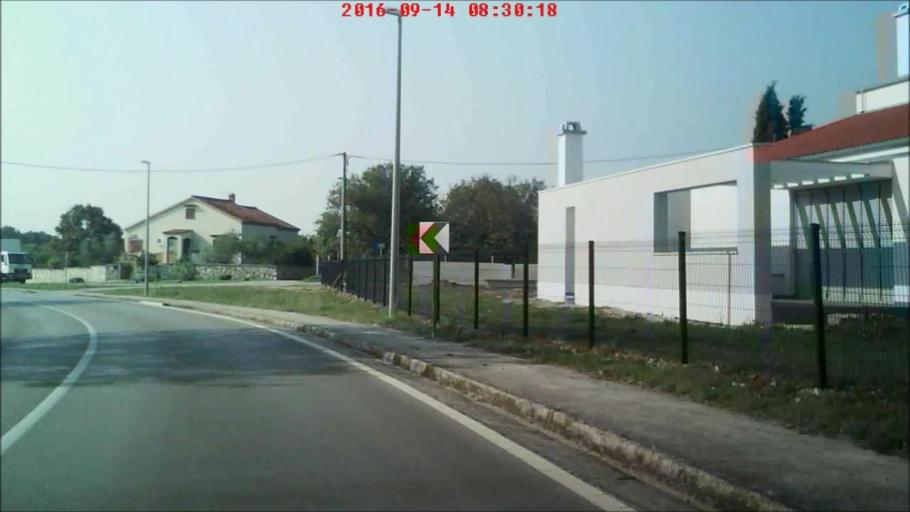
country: HR
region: Zadarska
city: Zadar
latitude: 44.1739
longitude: 15.2887
